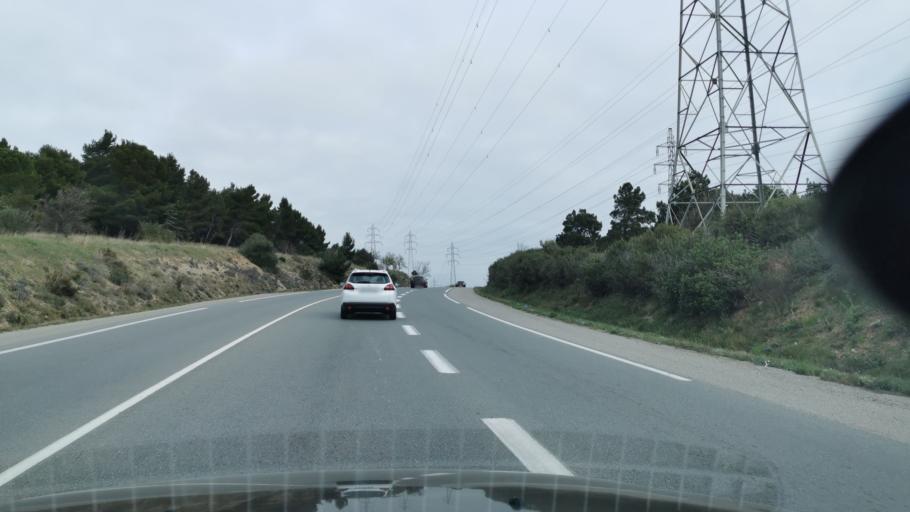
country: FR
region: Languedoc-Roussillon
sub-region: Departement de l'Aude
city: Narbonne
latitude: 43.1829
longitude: 2.9681
